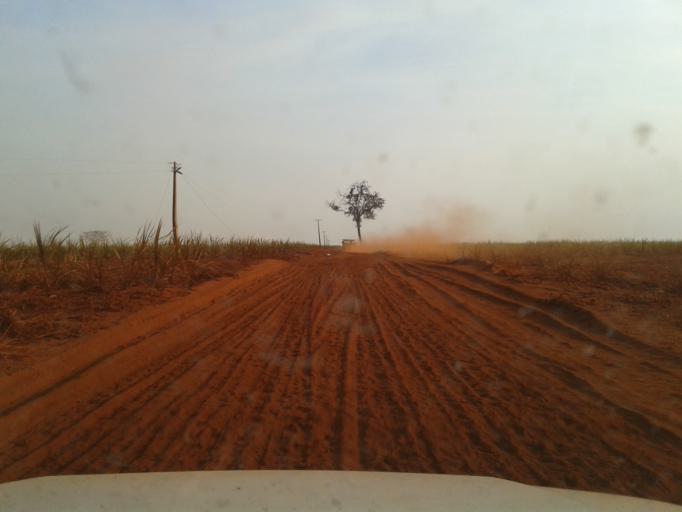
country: BR
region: Minas Gerais
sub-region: Capinopolis
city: Capinopolis
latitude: -18.7321
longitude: -49.6867
